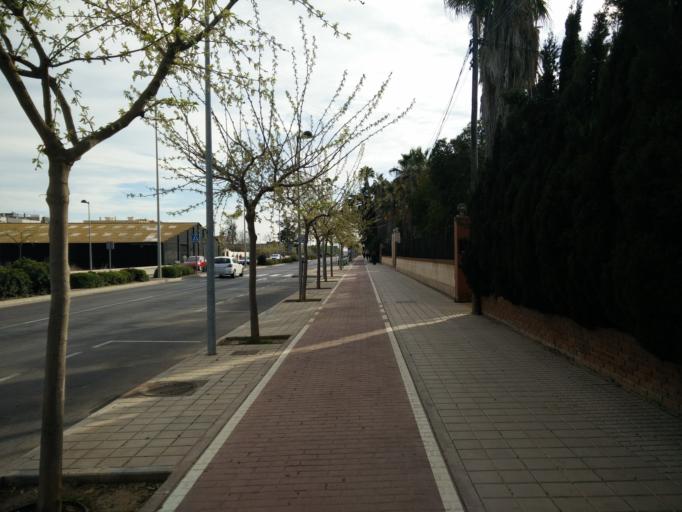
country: ES
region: Valencia
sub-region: Provincia de Castello
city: Castello de la Plana
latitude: 39.9816
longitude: -0.0531
